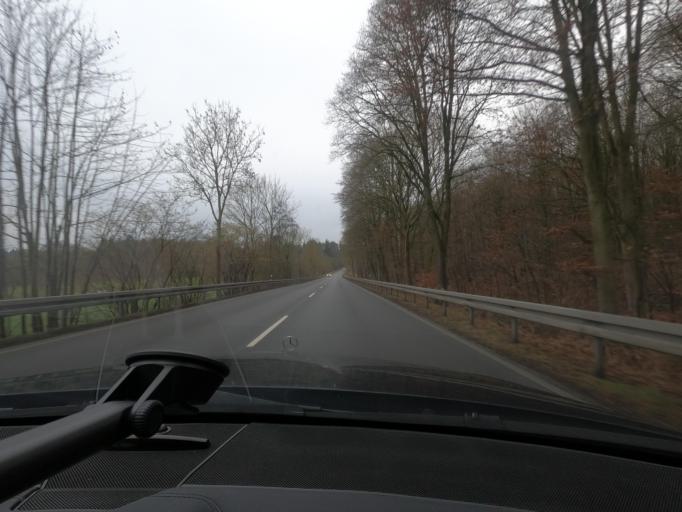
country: DE
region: Hesse
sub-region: Regierungsbezirk Kassel
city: Bad Arolsen
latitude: 51.4165
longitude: 9.0187
